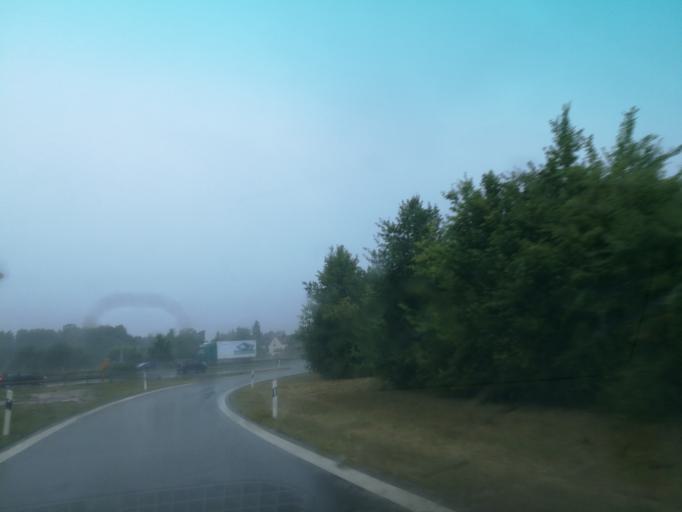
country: DE
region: Bavaria
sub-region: Regierungsbezirk Mittelfranken
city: Erlangen
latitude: 49.5425
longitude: 10.9939
